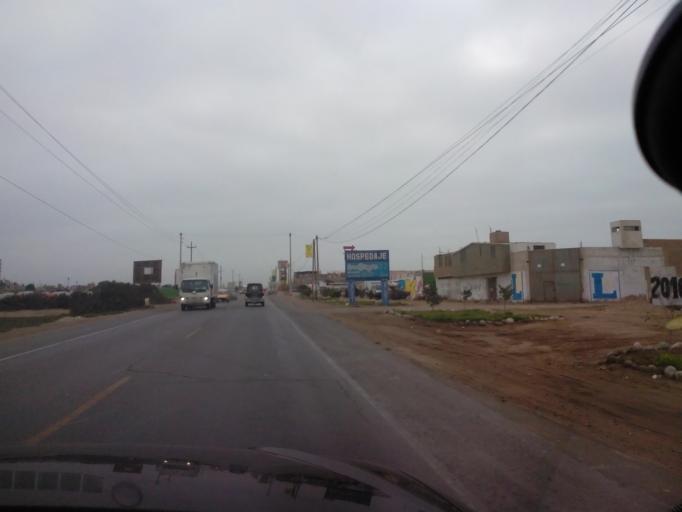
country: PE
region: Ica
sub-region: Provincia de Pisco
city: Villa Tupac Amaru
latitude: -13.7088
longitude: -76.1521
